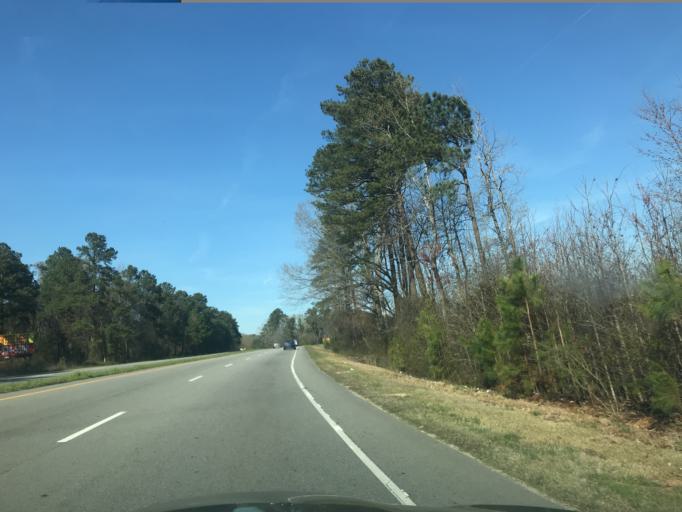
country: US
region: North Carolina
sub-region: Wake County
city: Garner
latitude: 35.6750
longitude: -78.6893
